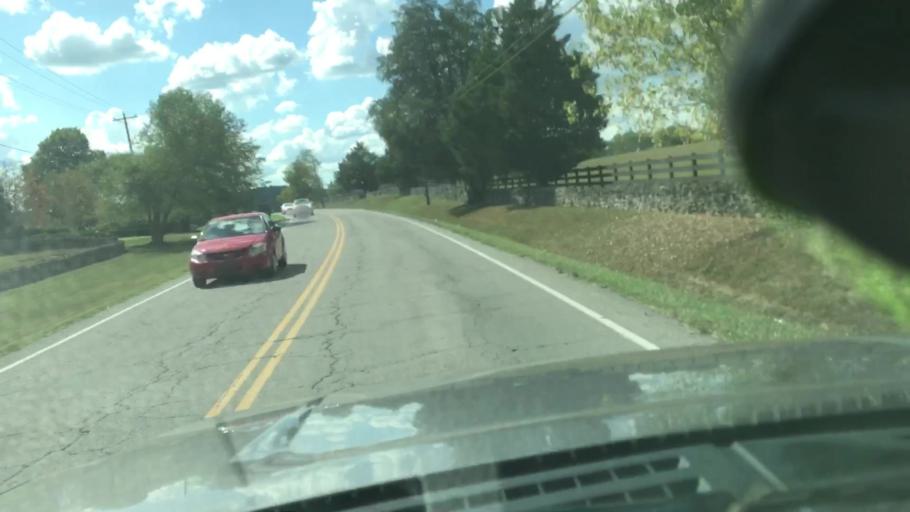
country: US
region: Tennessee
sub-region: Davidson County
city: Forest Hills
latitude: 36.0284
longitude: -86.9107
